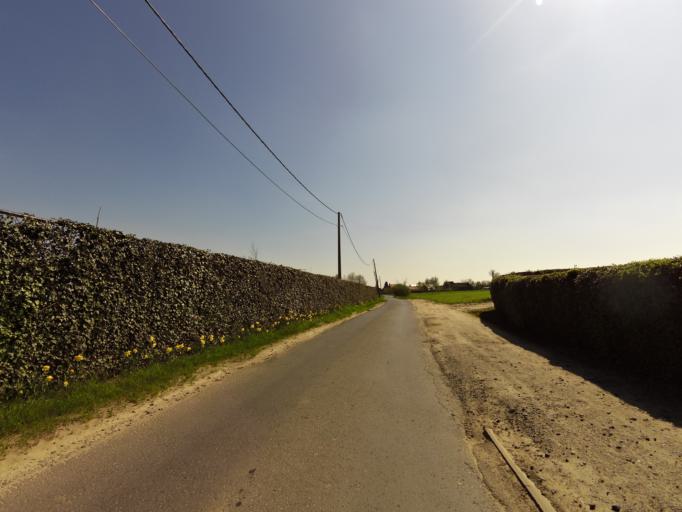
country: BE
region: Flanders
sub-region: Provincie West-Vlaanderen
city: Kortemark
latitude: 51.0585
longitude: 3.0200
